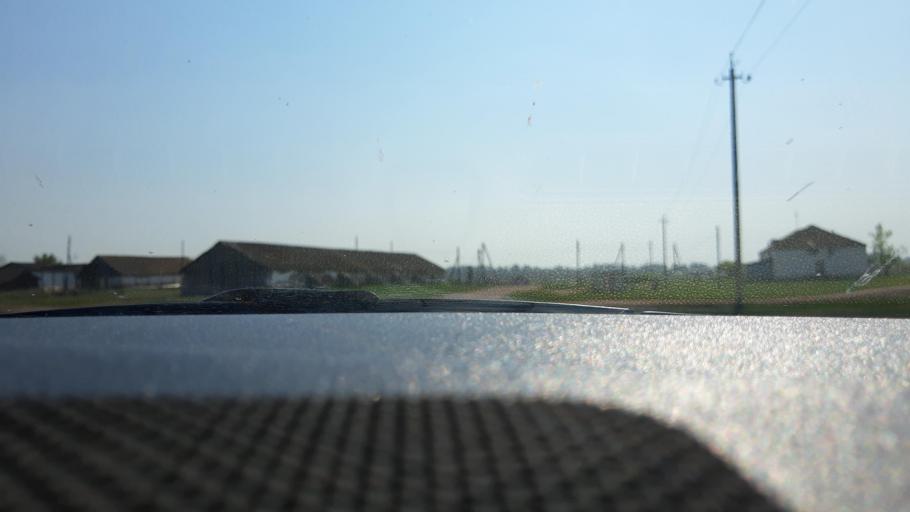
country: RU
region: Bashkortostan
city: Chishmy
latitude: 54.4483
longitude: 55.3198
